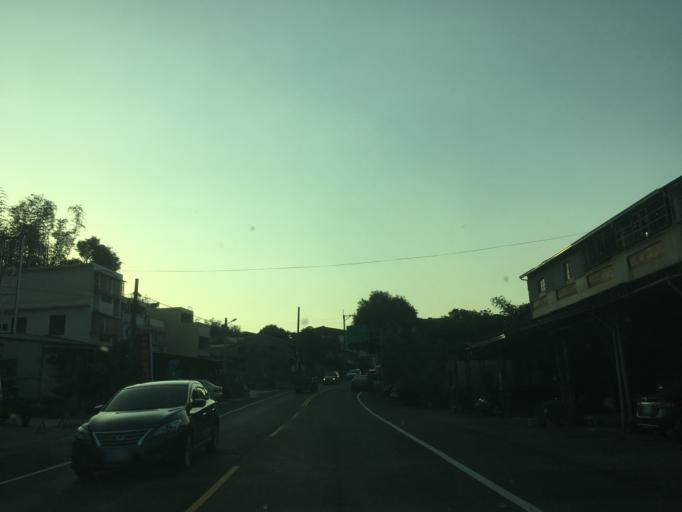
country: TW
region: Taiwan
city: Zhongxing New Village
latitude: 23.9508
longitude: 120.6575
